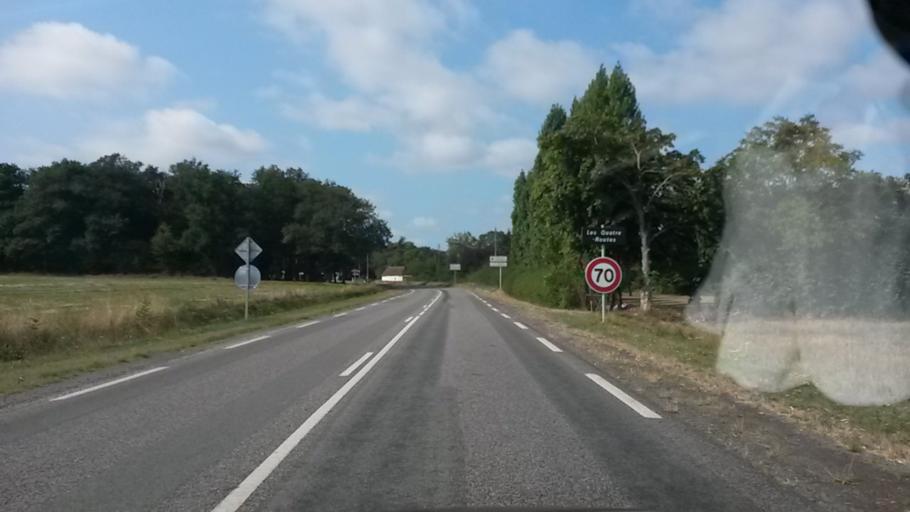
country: FR
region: Haute-Normandie
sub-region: Departement de l'Eure
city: Damville
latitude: 48.8253
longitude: 1.0100
